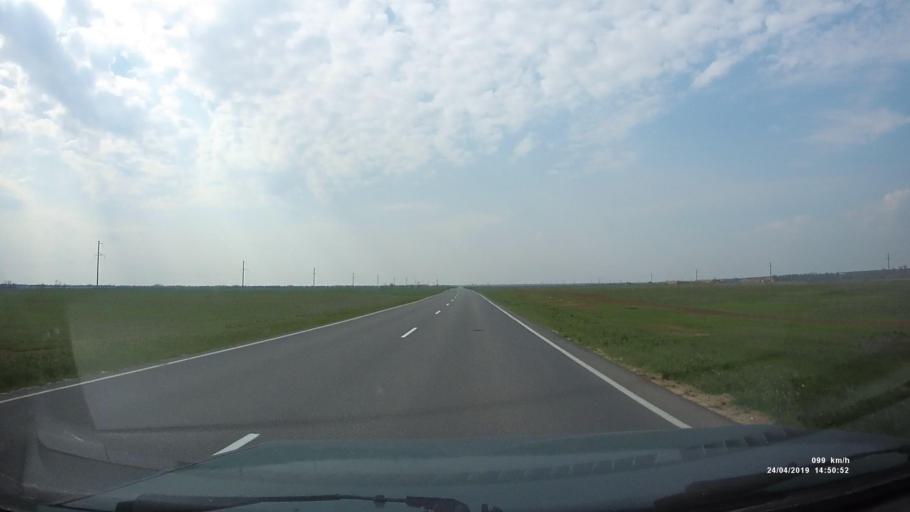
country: RU
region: Rostov
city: Remontnoye
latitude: 46.5206
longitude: 43.7115
